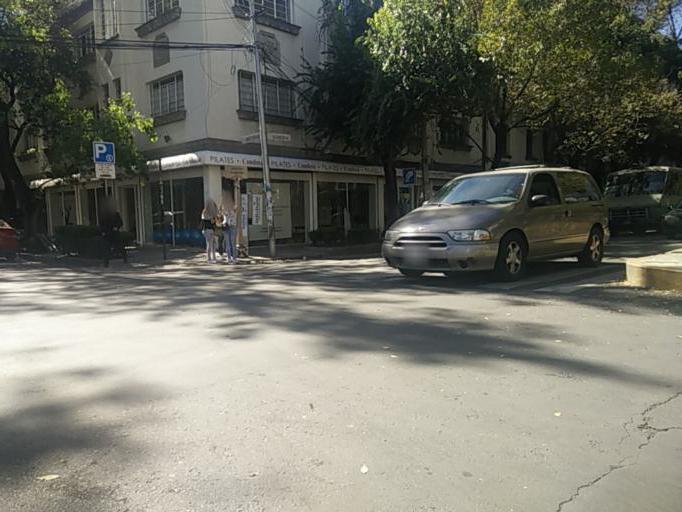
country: MX
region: Mexico City
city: Benito Juarez
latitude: 19.4130
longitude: -99.1672
